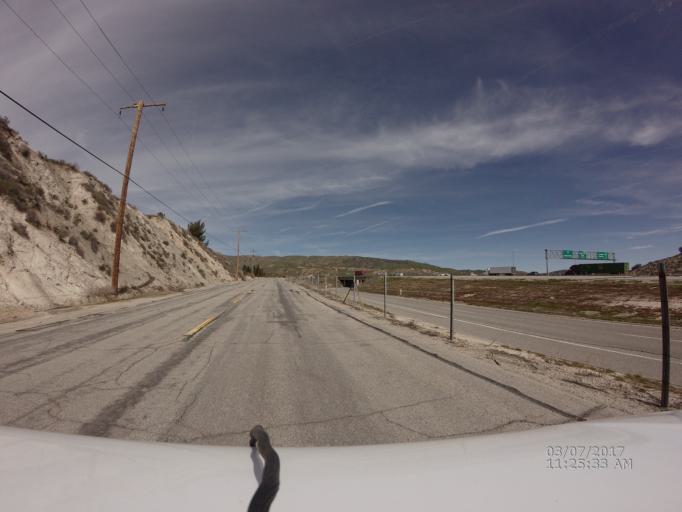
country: US
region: California
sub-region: Kern County
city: Lebec
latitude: 34.7562
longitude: -118.7966
